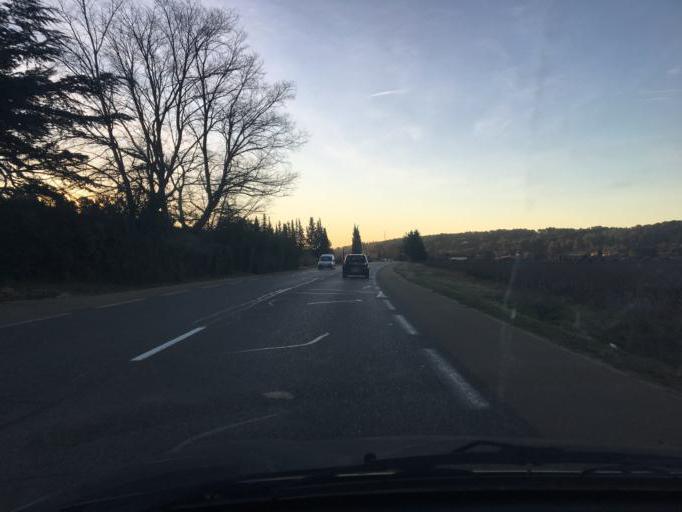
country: FR
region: Provence-Alpes-Cote d'Azur
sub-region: Departement du Var
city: Lorgues
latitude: 43.4822
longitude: 6.3701
